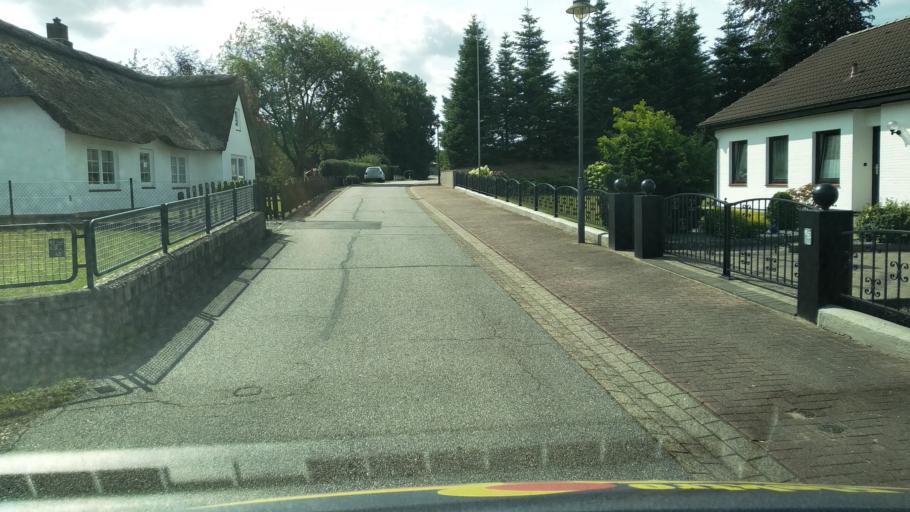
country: DE
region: Schleswig-Holstein
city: Brekendorf
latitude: 54.4192
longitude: 9.6378
